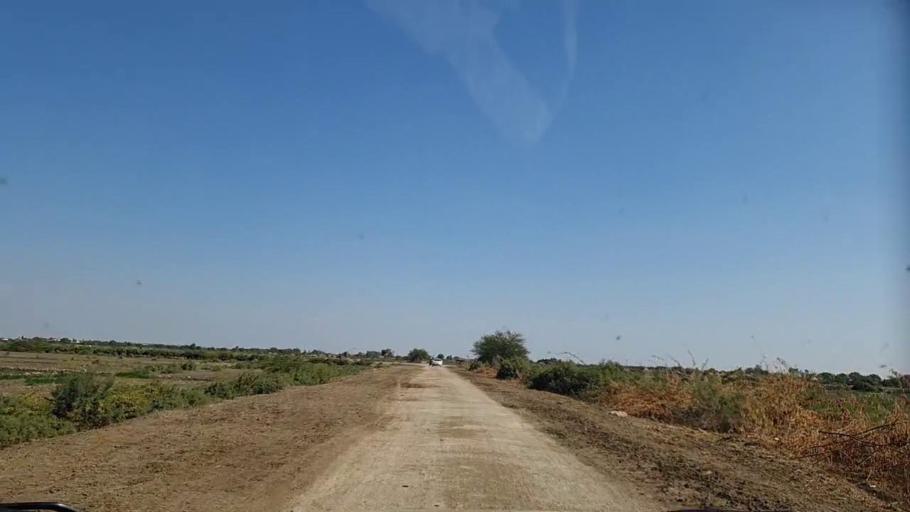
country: PK
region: Sindh
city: Pithoro
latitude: 25.6862
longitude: 69.4769
